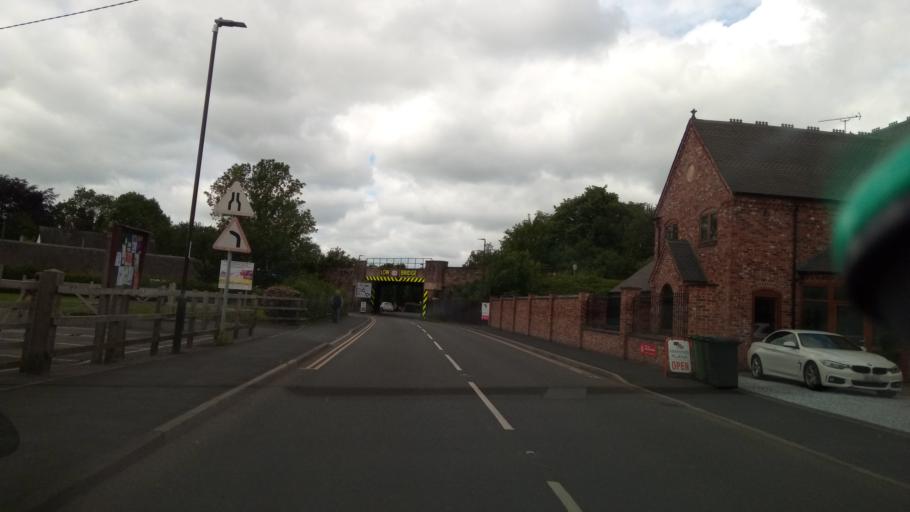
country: GB
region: England
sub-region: Derbyshire
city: Repton
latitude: 52.8537
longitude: -1.5620
